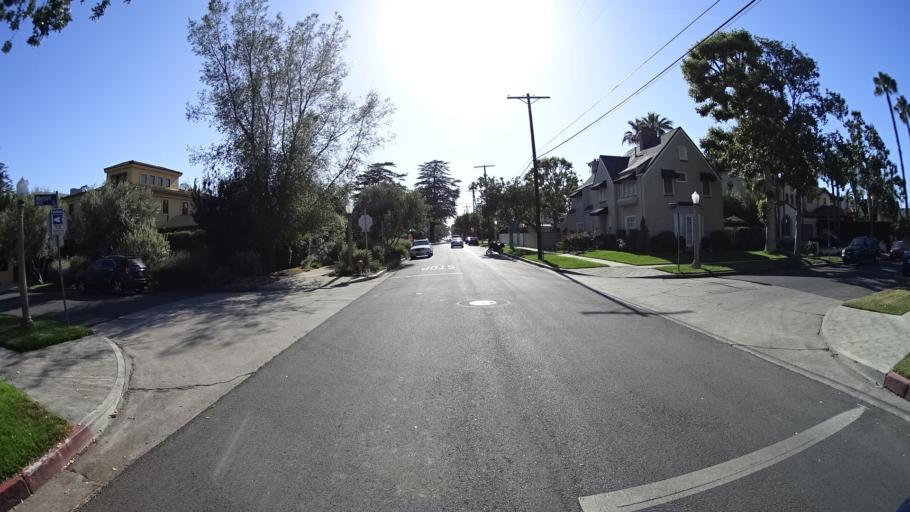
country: US
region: California
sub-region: Los Angeles County
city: Universal City
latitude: 34.1504
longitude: -118.3495
